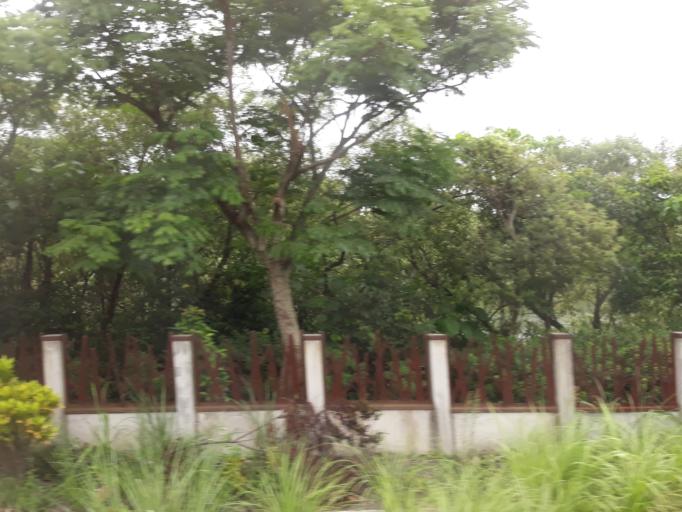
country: TW
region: Taiwan
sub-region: Yilan
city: Yilan
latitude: 24.6816
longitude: 121.7746
